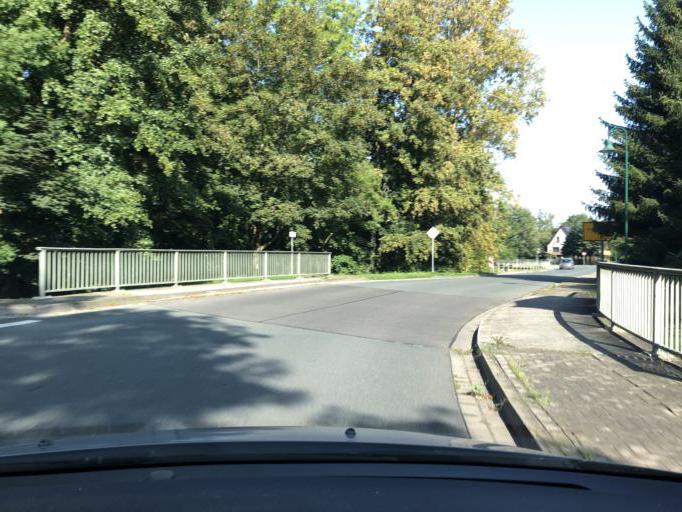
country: DE
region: Thuringia
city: Rastenberg
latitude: 51.2008
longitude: 11.4590
